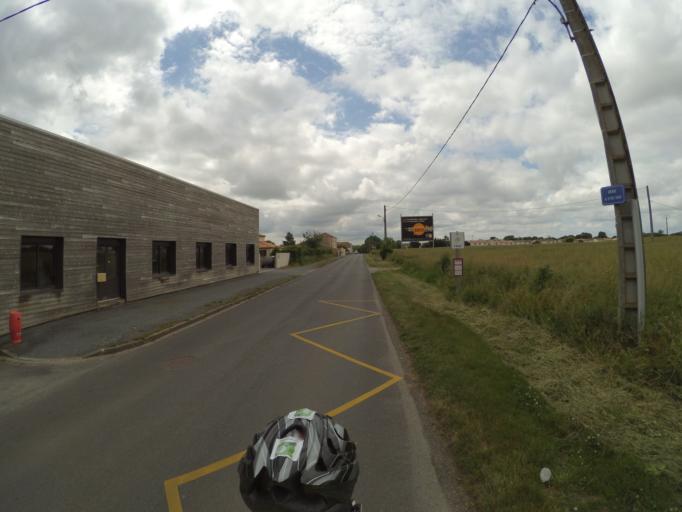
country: FR
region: Poitou-Charentes
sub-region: Departement de la Charente-Maritime
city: Breuil-Magne
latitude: 45.9615
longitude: -0.9698
